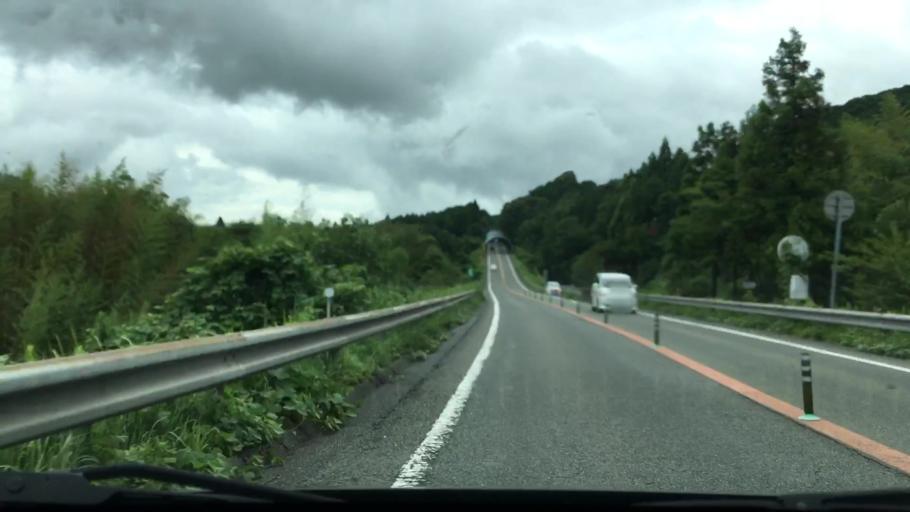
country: JP
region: Hyogo
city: Nishiwaki
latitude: 35.0828
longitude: 134.7744
